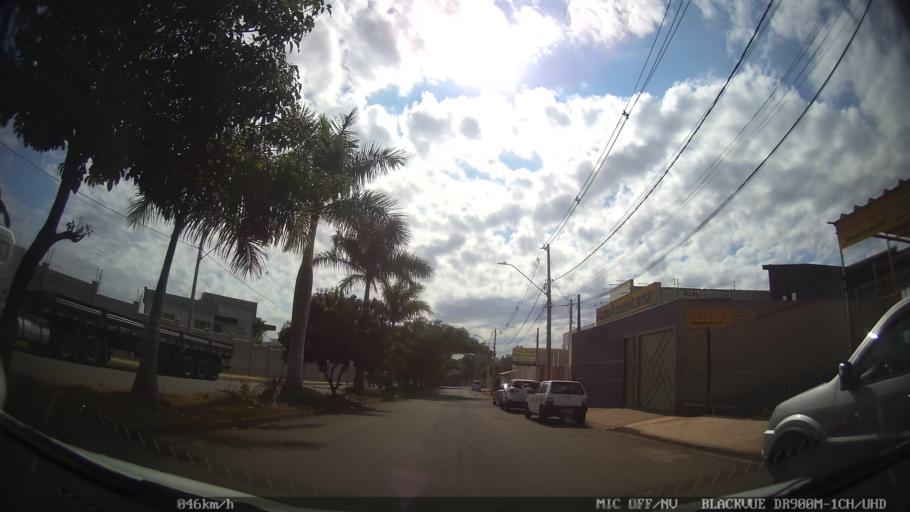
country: BR
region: Sao Paulo
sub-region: Americana
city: Americana
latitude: -22.7187
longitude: -47.3231
